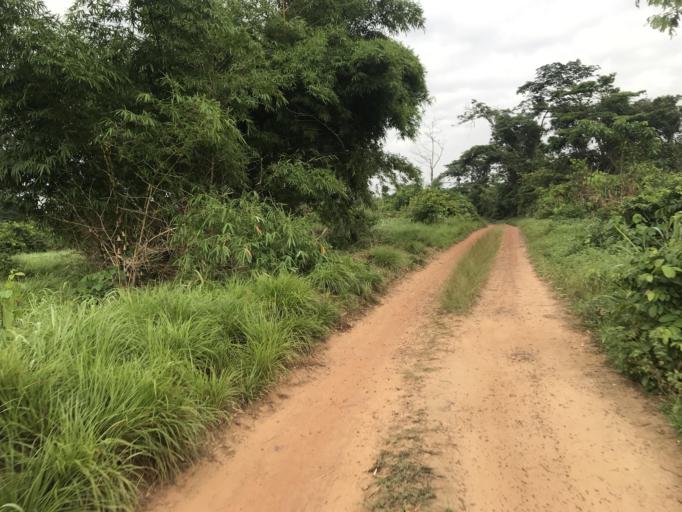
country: SL
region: Eastern Province
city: Pendembu
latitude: 8.0894
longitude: -10.6950
